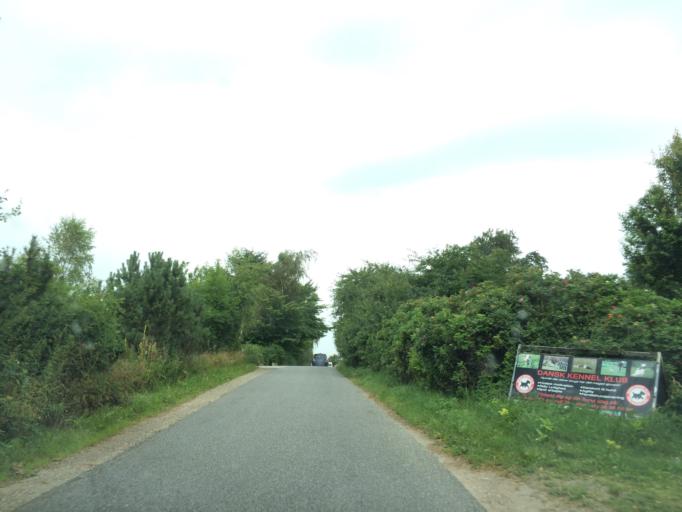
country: DK
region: Central Jutland
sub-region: Syddjurs Kommune
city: Ronde
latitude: 56.2409
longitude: 10.5553
